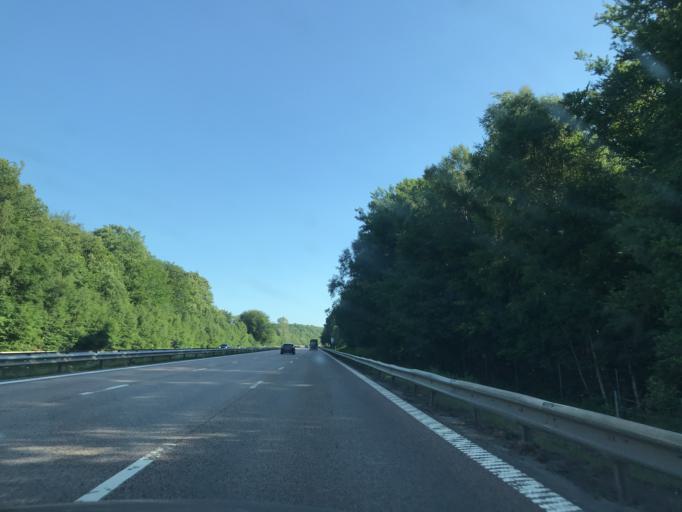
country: SE
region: Skane
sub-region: Angelholms Kommun
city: Munka-Ljungby
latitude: 56.3294
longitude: 12.9151
